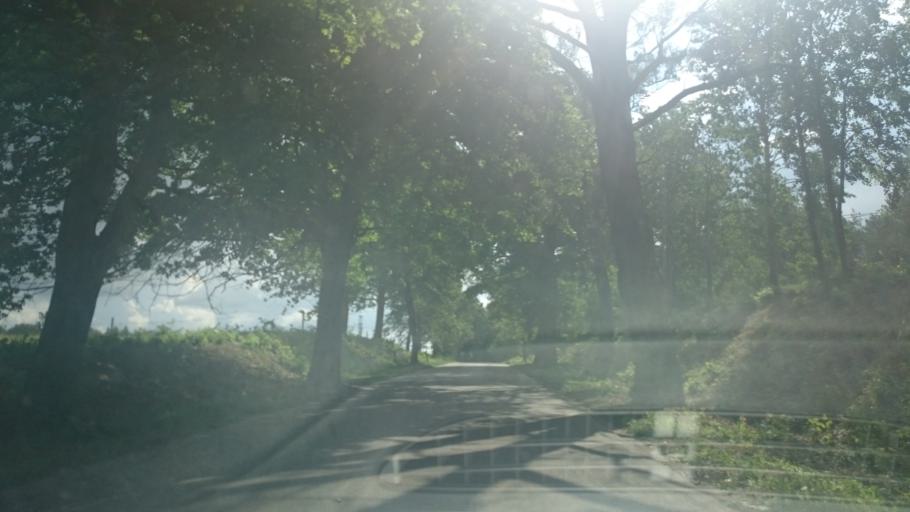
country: PL
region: Pomeranian Voivodeship
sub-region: Powiat starogardzki
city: Kaliska
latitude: 53.9685
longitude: 18.2476
